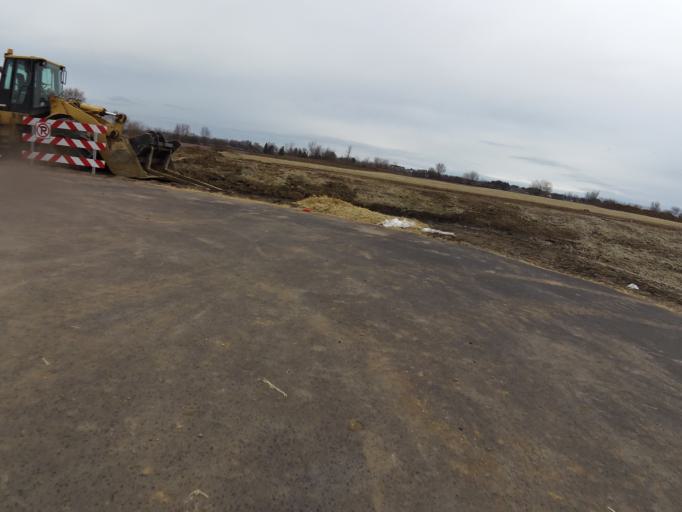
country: US
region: Minnesota
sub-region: Washington County
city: Lake Elmo
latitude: 44.9993
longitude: -92.8668
